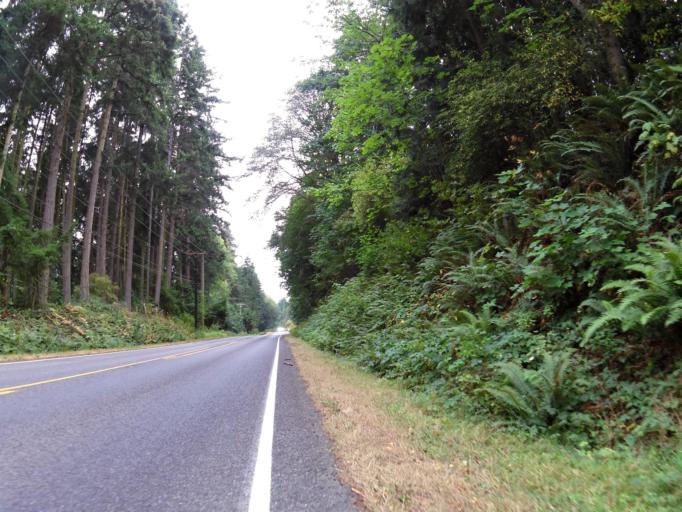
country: US
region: Washington
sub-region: Jefferson County
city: Port Hadlock-Irondale
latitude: 48.0130
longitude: -122.7296
